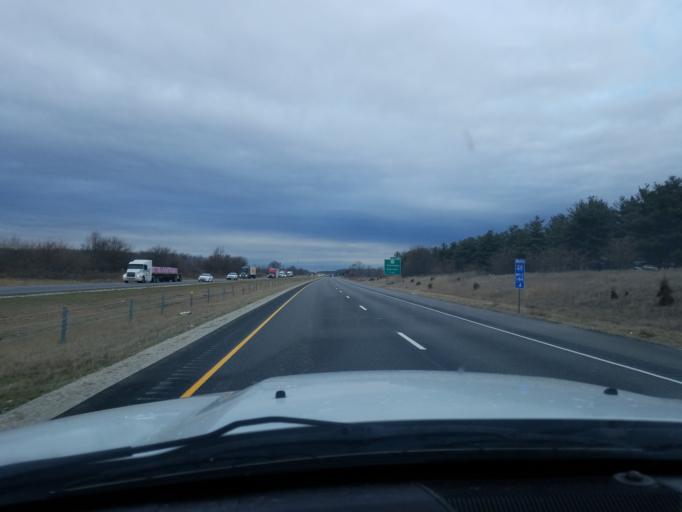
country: US
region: Indiana
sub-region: Boone County
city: Lebanon
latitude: 40.1060
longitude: -86.5113
